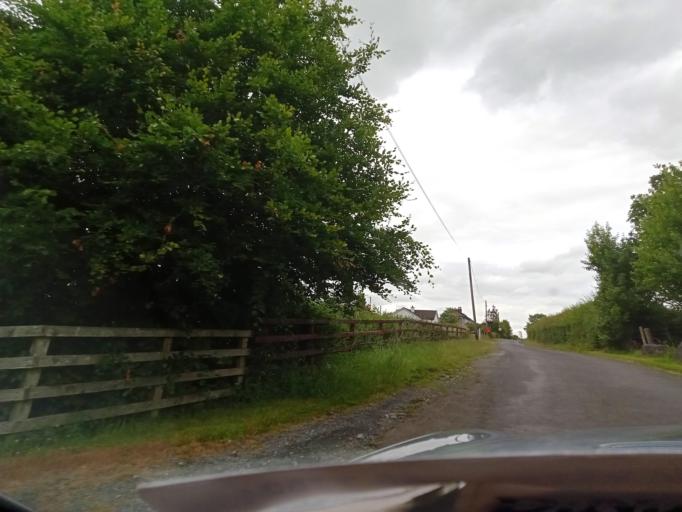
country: IE
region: Leinster
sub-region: Kilkenny
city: Thomastown
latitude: 52.5522
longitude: -7.2151
